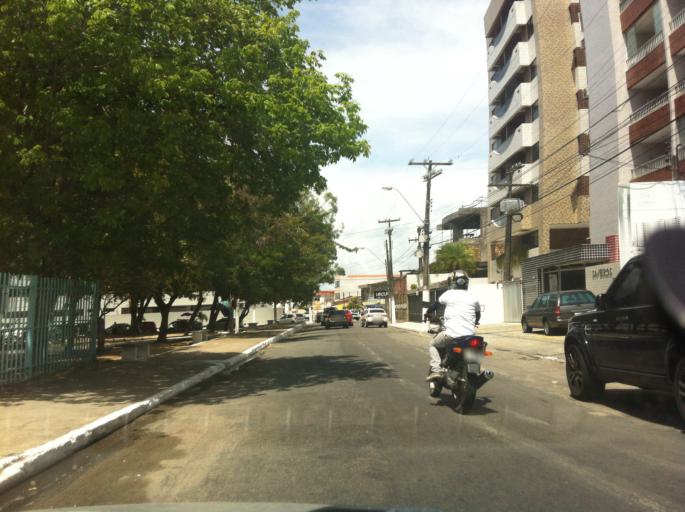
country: BR
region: Alagoas
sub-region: Maceio
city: Maceio
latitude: -9.6624
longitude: -35.7091
